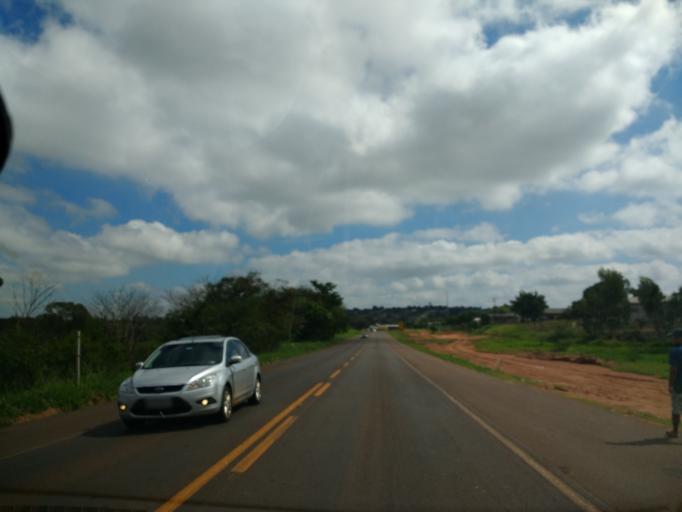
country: BR
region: Parana
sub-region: Cruzeiro Do Oeste
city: Cruzeiro do Oeste
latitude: -23.7922
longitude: -53.0727
